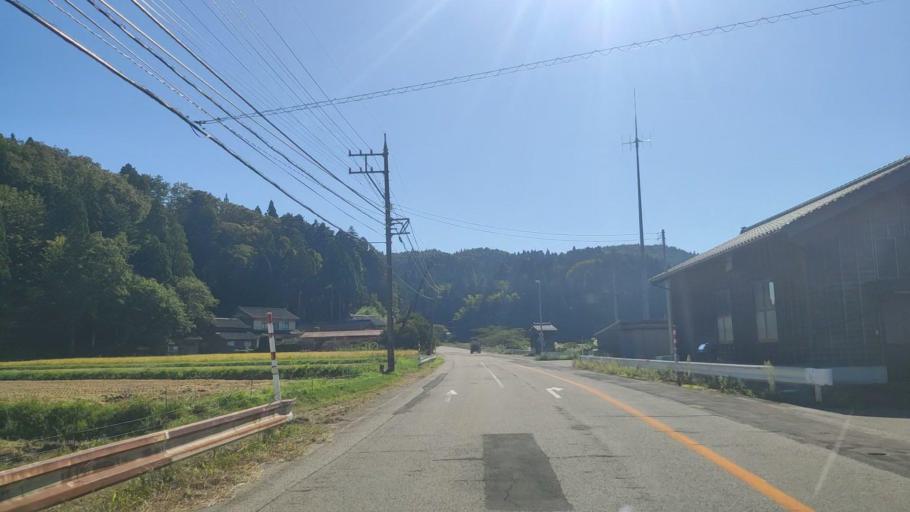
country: JP
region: Ishikawa
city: Nanao
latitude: 37.3358
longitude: 137.2093
